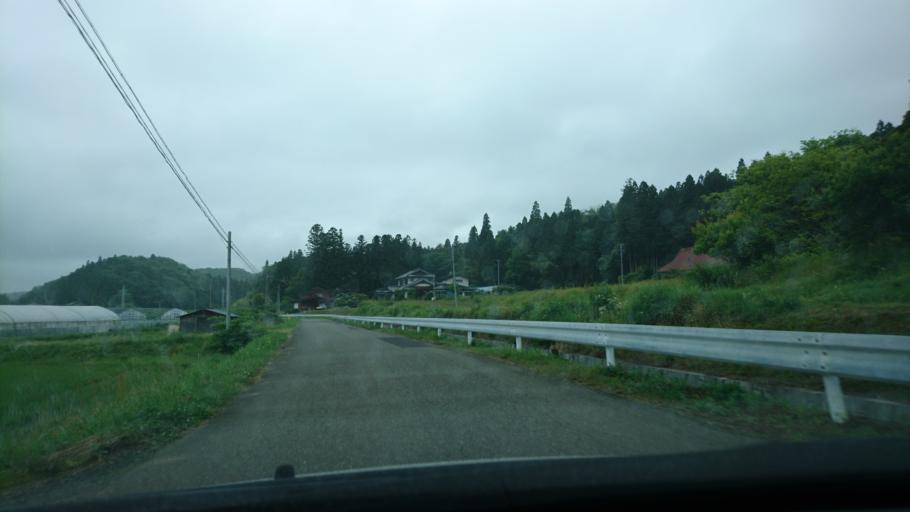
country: JP
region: Iwate
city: Ichinoseki
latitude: 38.9518
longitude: 141.0455
